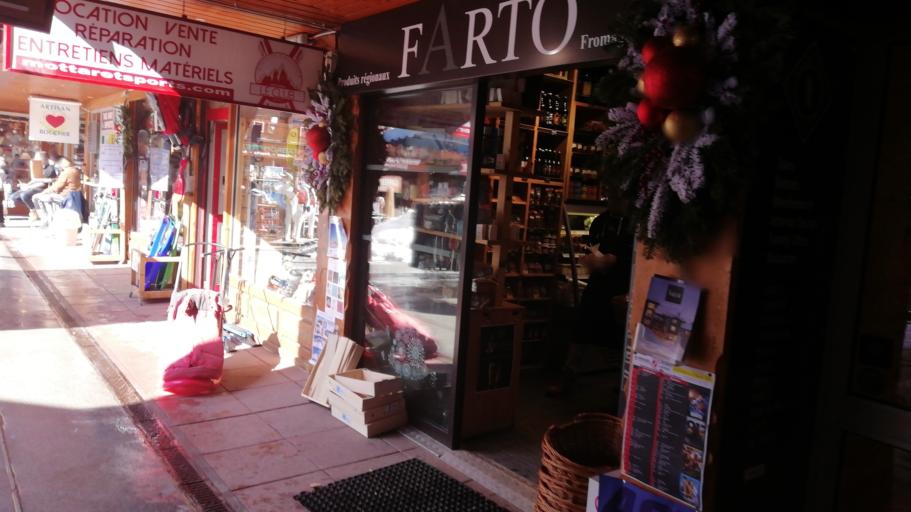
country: FR
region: Rhone-Alpes
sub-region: Departement de la Savoie
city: Meribel
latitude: 45.3733
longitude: 6.5799
